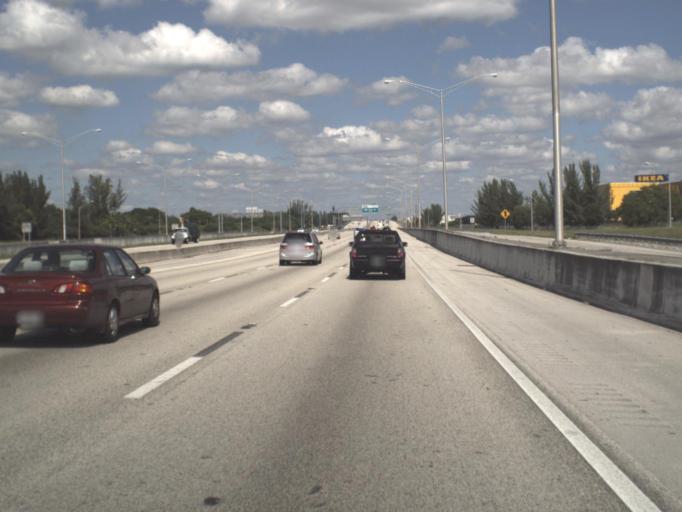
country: US
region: Florida
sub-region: Miami-Dade County
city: Sweetwater
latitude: 25.7859
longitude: -80.3858
